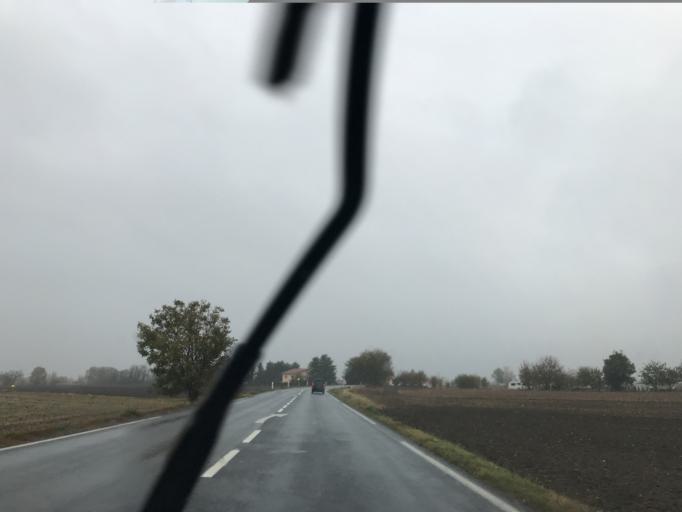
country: FR
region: Auvergne
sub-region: Departement du Puy-de-Dome
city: Dallet
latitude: 45.7830
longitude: 3.2487
